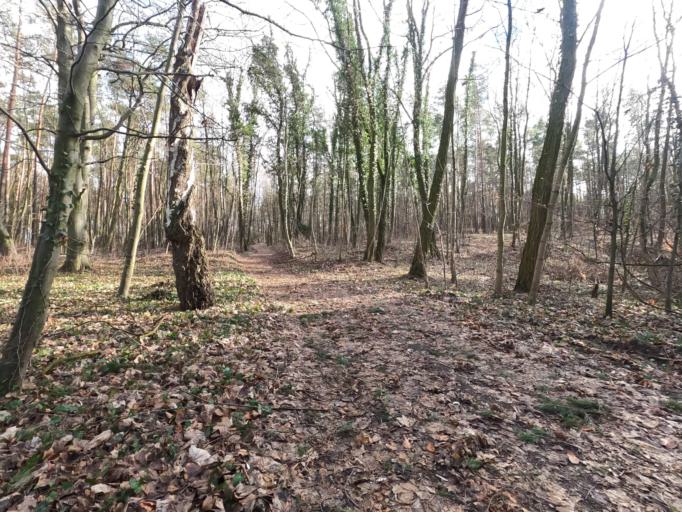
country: PL
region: Greater Poland Voivodeship
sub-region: Powiat pilski
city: Miasteczko Krajenskie
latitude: 53.1017
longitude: 17.0315
